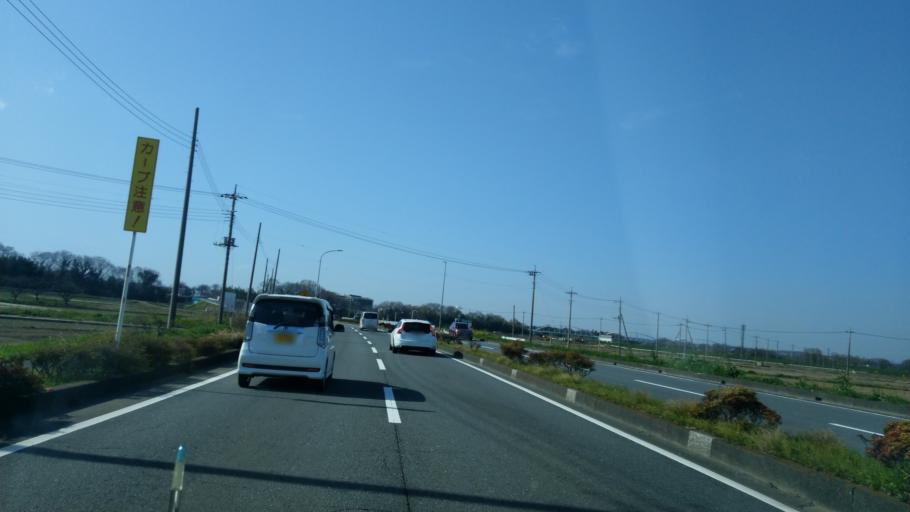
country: JP
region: Saitama
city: Sakado
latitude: 36.0068
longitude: 139.4448
